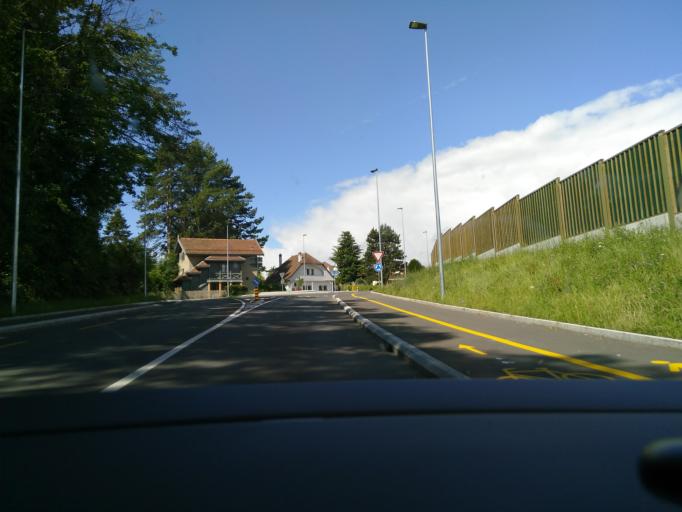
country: CH
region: Vaud
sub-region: Morges District
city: Morges
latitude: 46.5060
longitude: 6.4804
